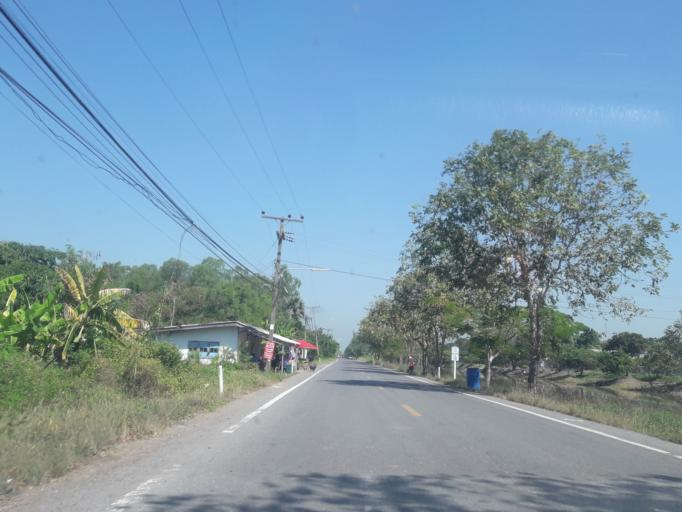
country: TH
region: Pathum Thani
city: Nong Suea
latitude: 14.1506
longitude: 100.8459
